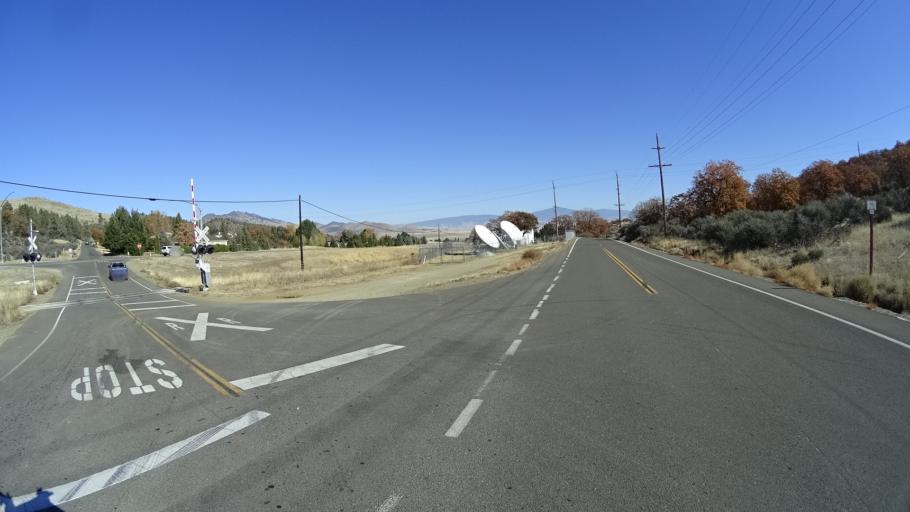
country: US
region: California
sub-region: Siskiyou County
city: Yreka
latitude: 41.7388
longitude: -122.6149
